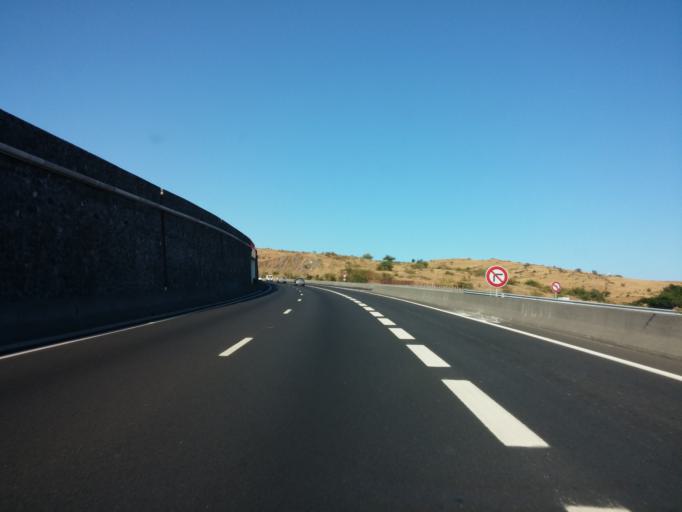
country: RE
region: Reunion
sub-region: Reunion
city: Saint-Paul
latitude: -21.0210
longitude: 55.2568
